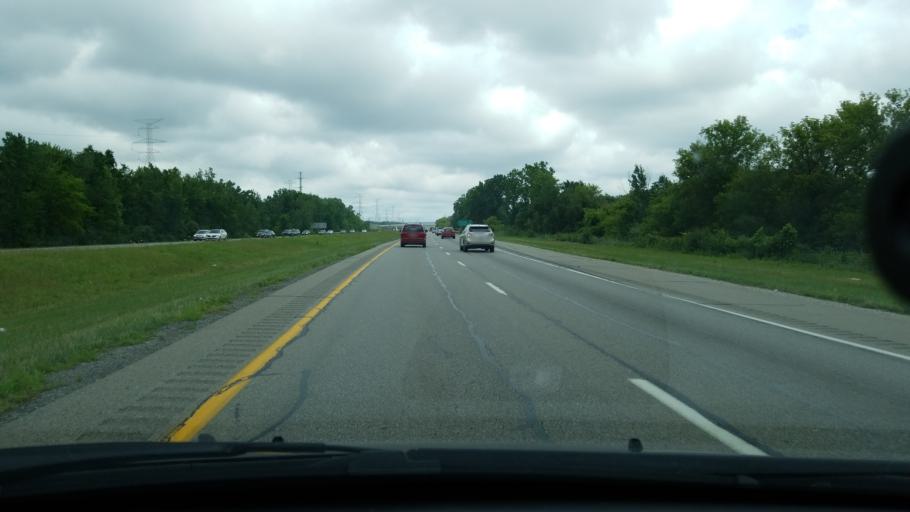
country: US
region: Ohio
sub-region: Lorain County
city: Sheffield
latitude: 41.4353
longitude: -82.0813
